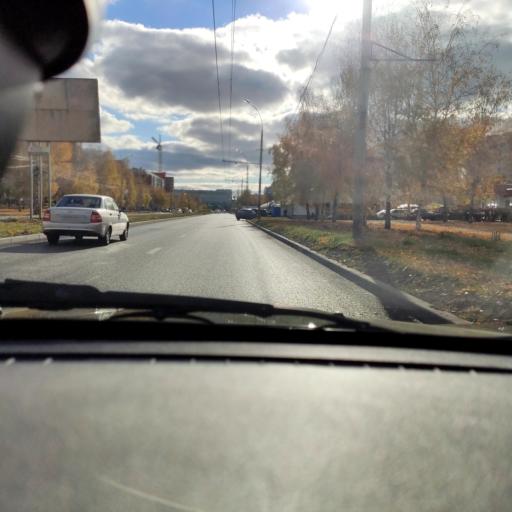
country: RU
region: Samara
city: Tol'yatti
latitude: 53.5314
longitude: 49.3279
